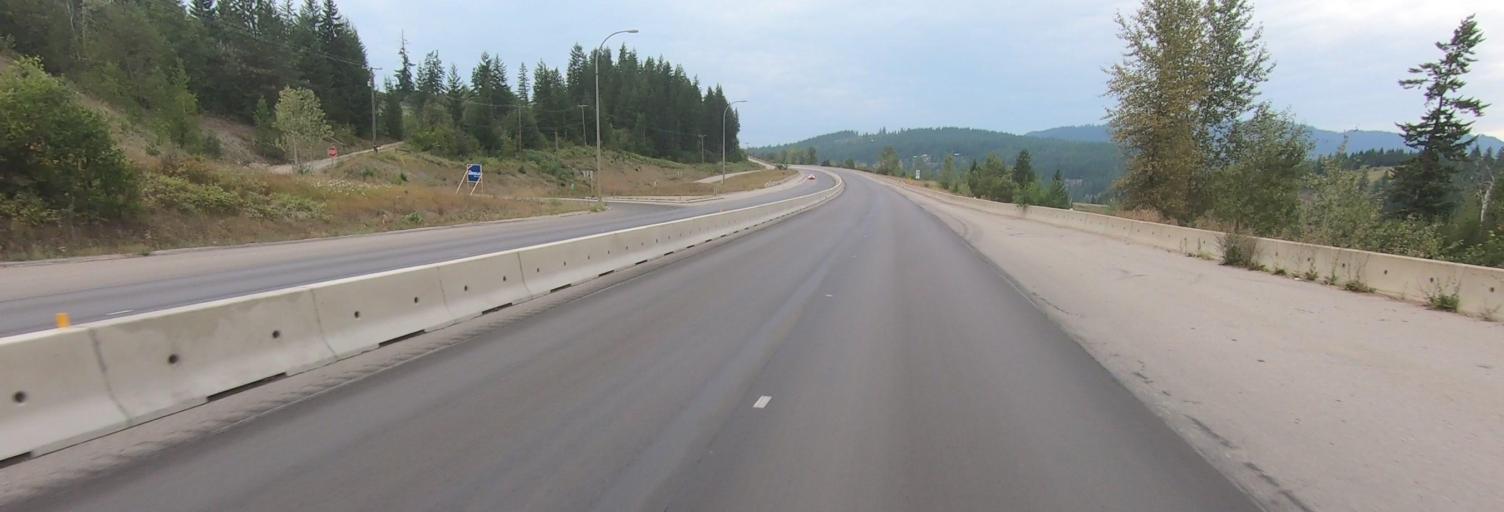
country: CA
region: British Columbia
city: Salmon Arm
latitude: 50.8400
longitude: -119.3278
